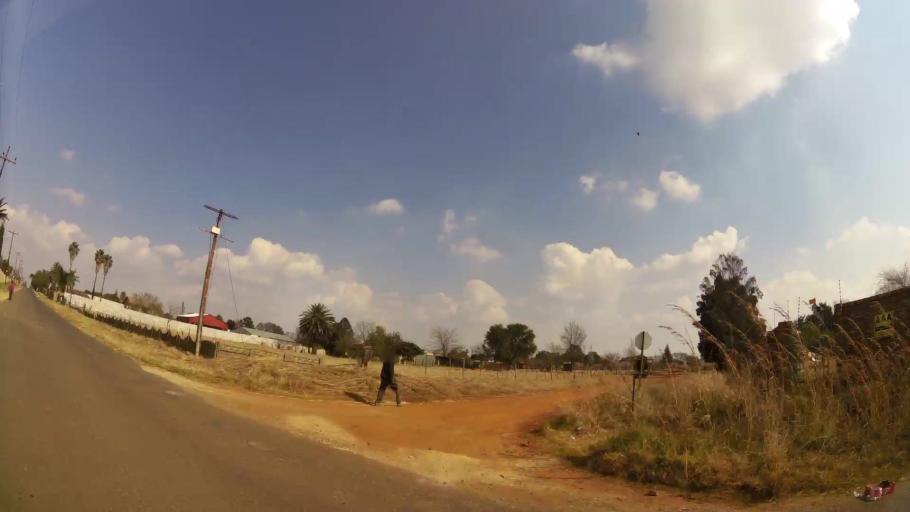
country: ZA
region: Mpumalanga
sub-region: Nkangala District Municipality
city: Delmas
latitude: -26.1849
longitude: 28.5402
